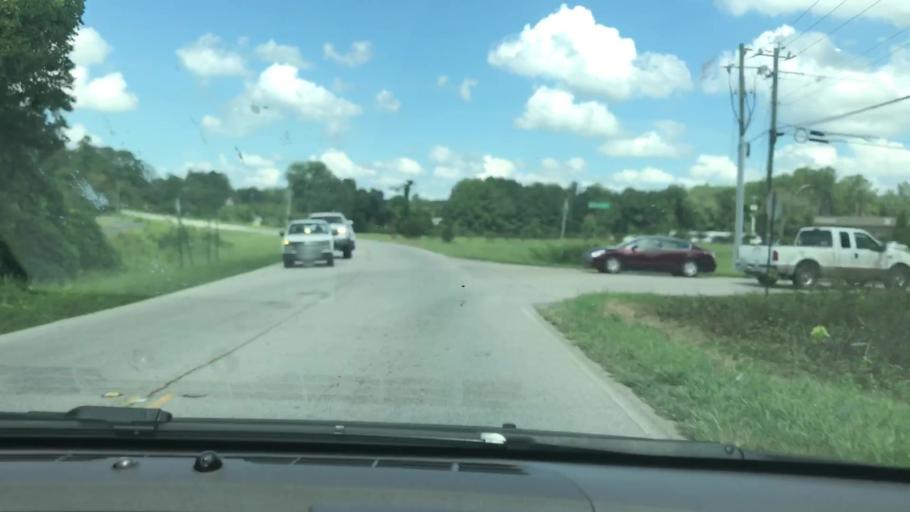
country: US
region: Georgia
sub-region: Troup County
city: La Grange
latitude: 33.0173
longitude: -85.0682
